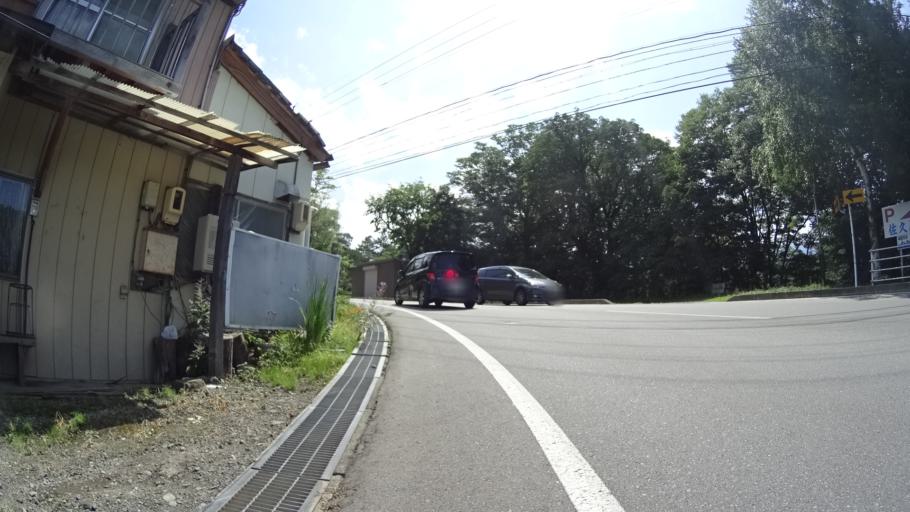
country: JP
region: Nagano
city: Saku
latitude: 36.0534
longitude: 138.4604
